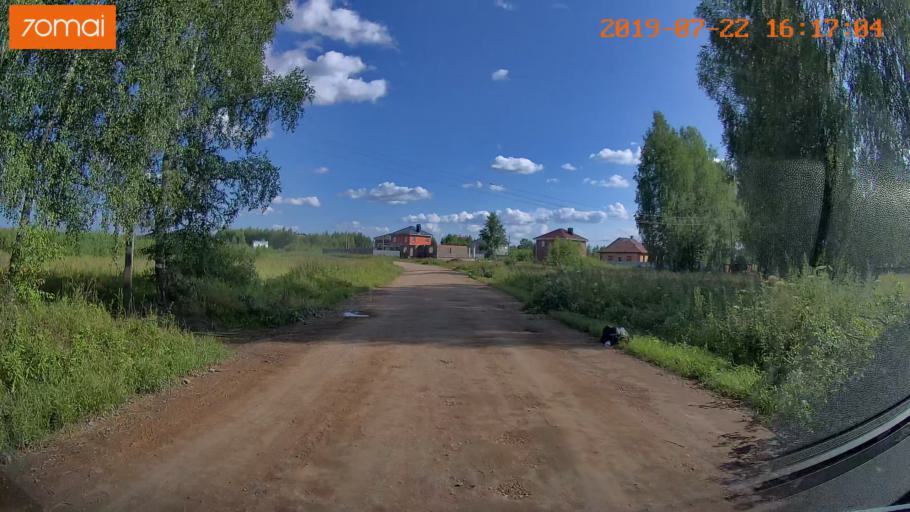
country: RU
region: Ivanovo
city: Novo-Talitsy
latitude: 57.0702
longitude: 40.8824
